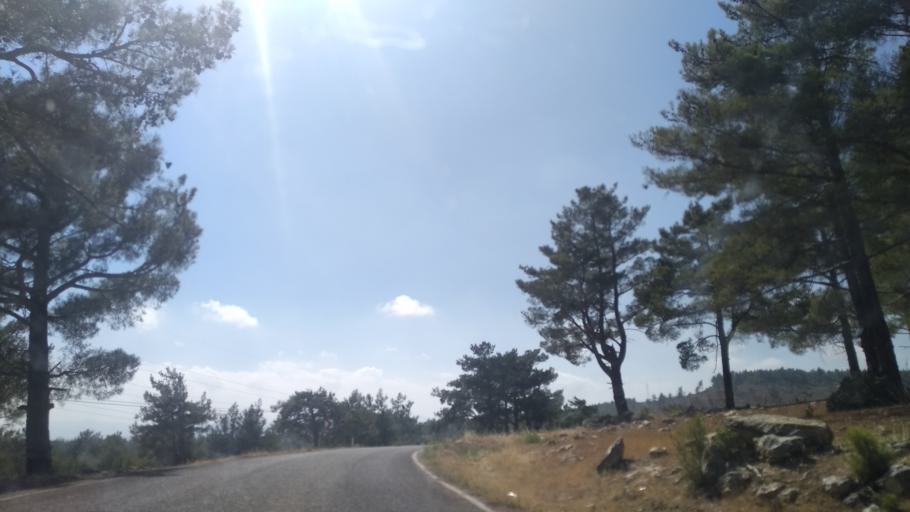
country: TR
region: Mersin
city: Gulnar
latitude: 36.3033
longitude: 33.4574
